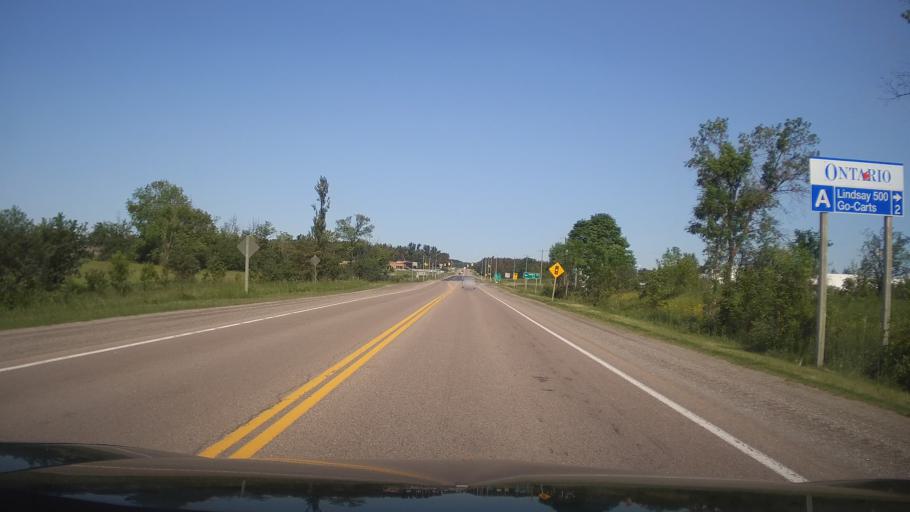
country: CA
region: Ontario
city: Omemee
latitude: 44.3449
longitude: -78.7708
